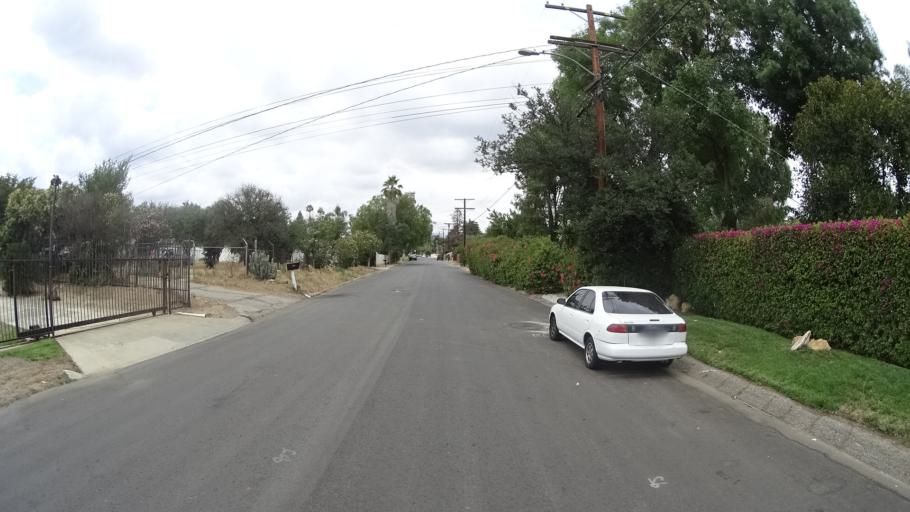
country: US
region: California
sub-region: Los Angeles County
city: San Fernando
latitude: 34.2480
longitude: -118.4631
